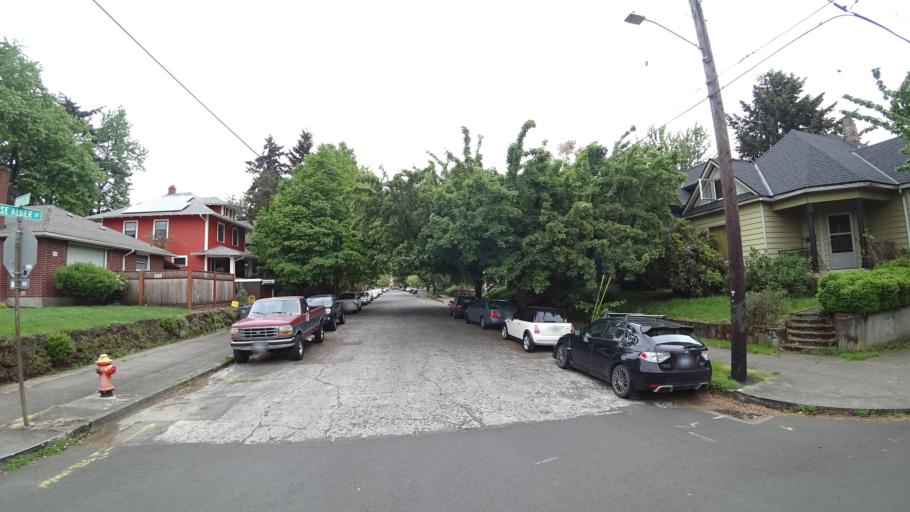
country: US
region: Oregon
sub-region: Multnomah County
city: Portland
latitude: 45.5179
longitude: -122.6258
